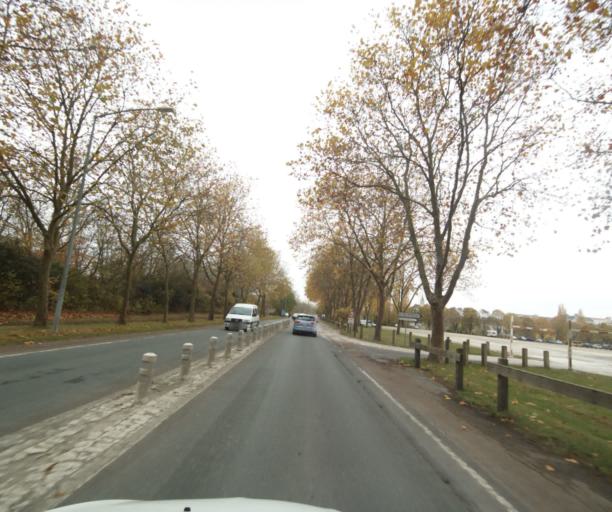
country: FR
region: Poitou-Charentes
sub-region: Departement de la Charente-Maritime
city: Saintes
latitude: 45.7408
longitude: -0.6289
